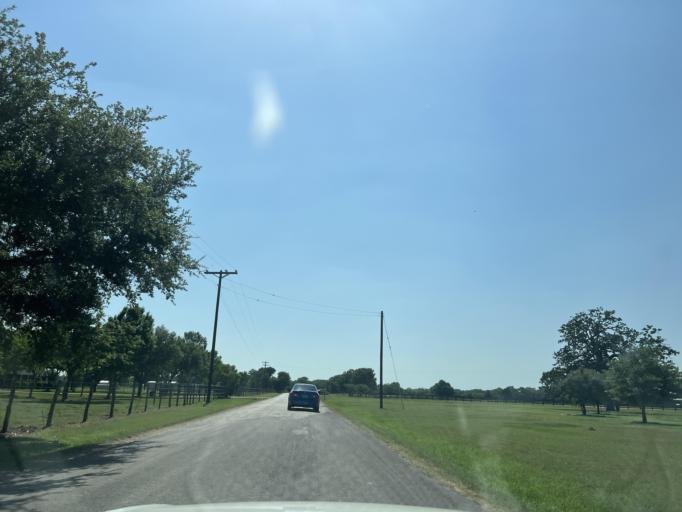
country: US
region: Texas
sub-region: Washington County
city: Brenham
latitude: 30.1565
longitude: -96.4982
